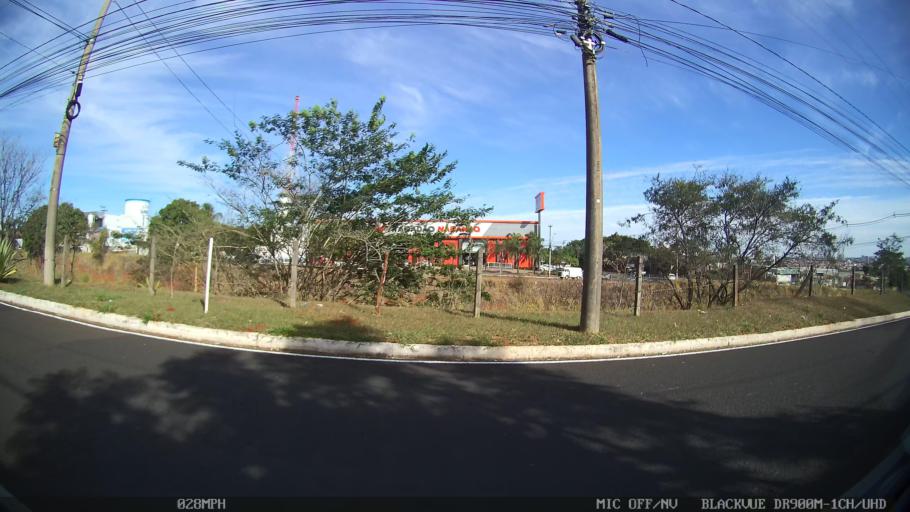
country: BR
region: Sao Paulo
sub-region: Sao Jose Do Rio Preto
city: Sao Jose do Rio Preto
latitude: -20.8014
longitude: -49.3484
